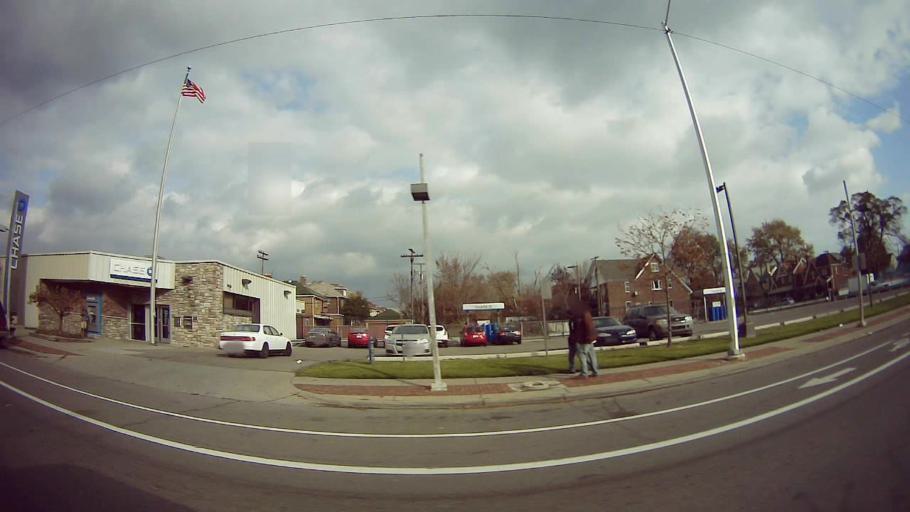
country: US
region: Michigan
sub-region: Wayne County
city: Highland Park
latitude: 42.3873
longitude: -83.1292
